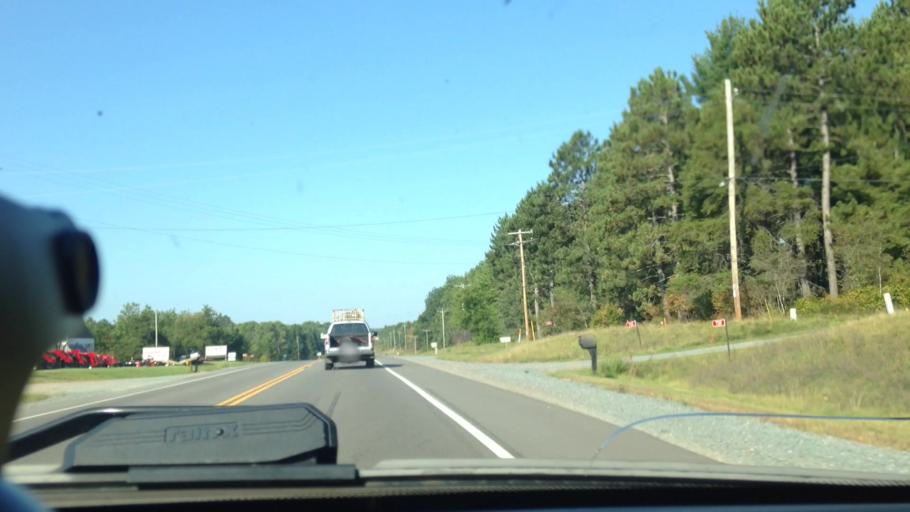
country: US
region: Michigan
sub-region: Dickinson County
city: Iron Mountain
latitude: 45.8761
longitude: -88.0932
